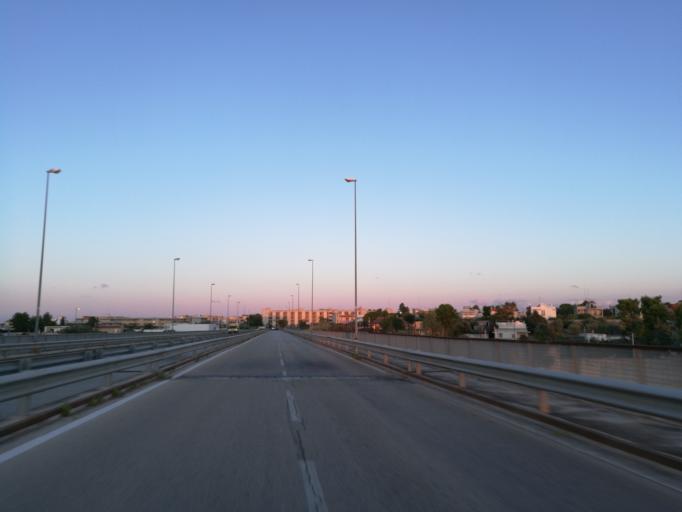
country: IT
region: Apulia
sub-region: Provincia di Bari
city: Loseto
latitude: 41.0672
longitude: 16.8586
